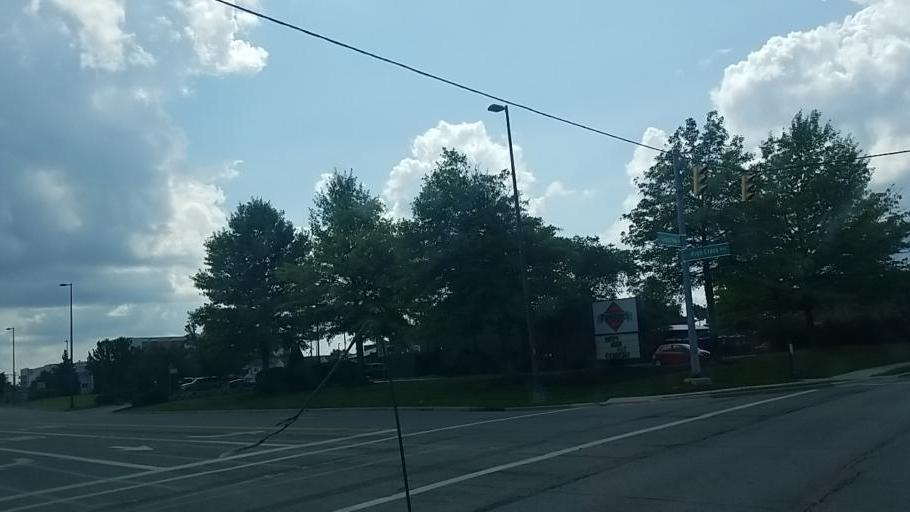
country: US
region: Ohio
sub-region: Franklin County
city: Worthington
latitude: 40.1183
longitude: -83.0122
